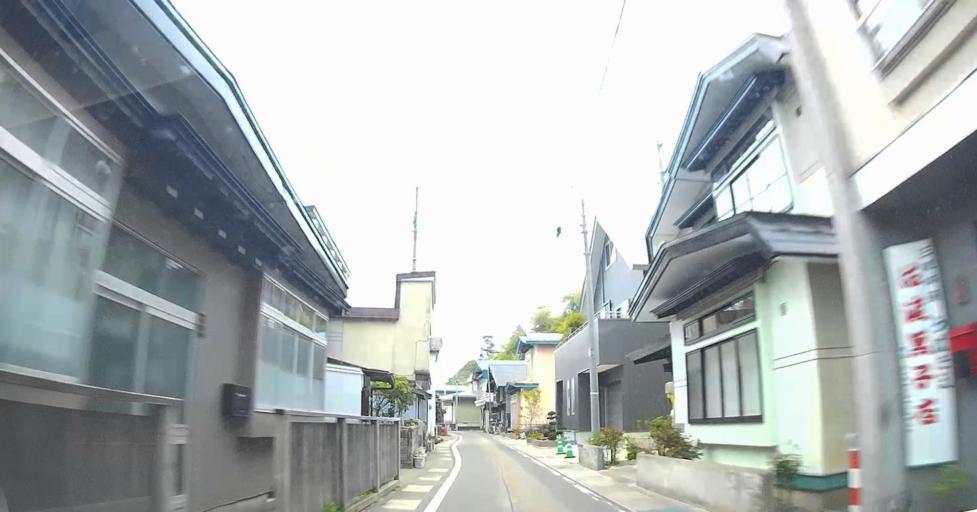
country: JP
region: Aomori
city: Shimokizukuri
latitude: 41.2017
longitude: 140.4290
